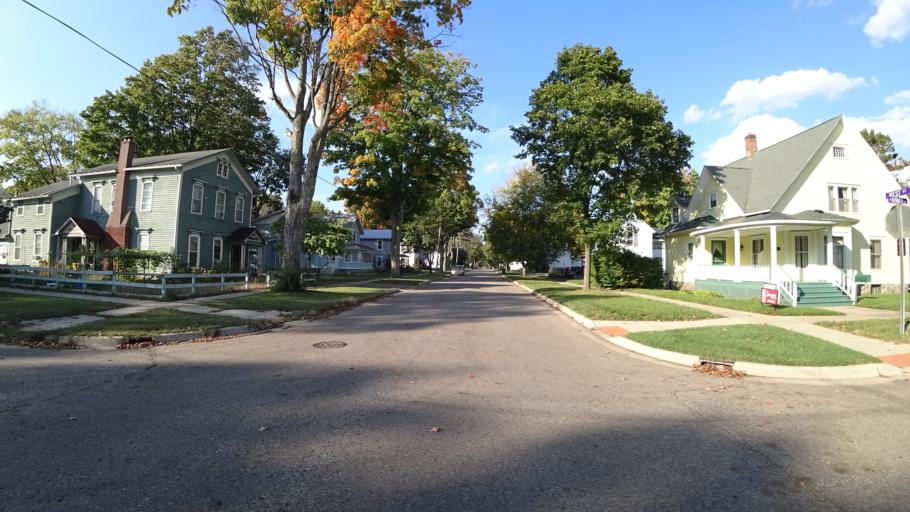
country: US
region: Michigan
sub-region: Saint Joseph County
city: Three Rivers
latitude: 41.9499
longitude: -85.6362
